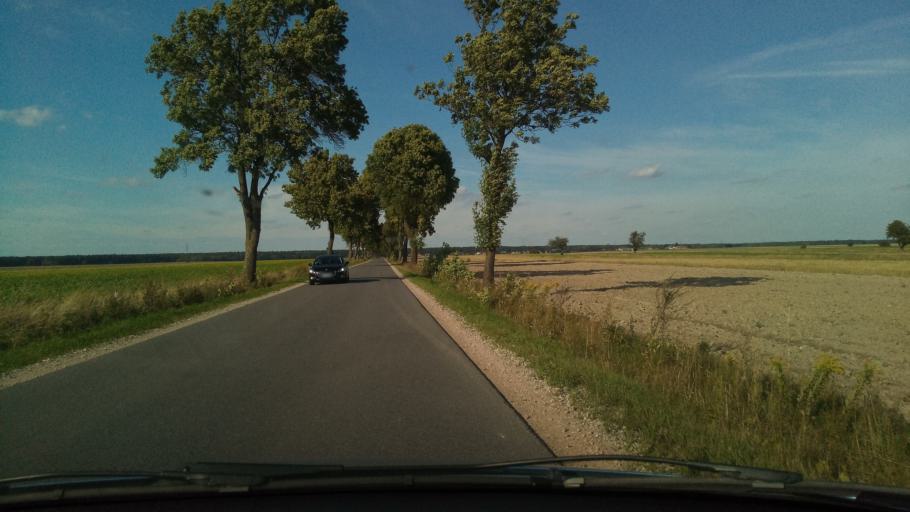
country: PL
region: Lodz Voivodeship
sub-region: Powiat piotrkowski
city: Sulejow
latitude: 51.3868
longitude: 19.8195
